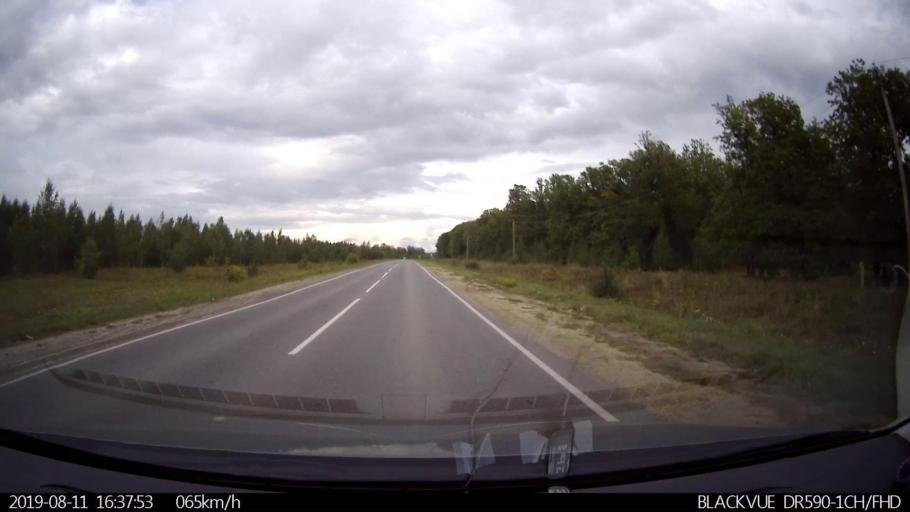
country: RU
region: Ulyanovsk
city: Mayna
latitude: 54.1310
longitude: 47.6179
